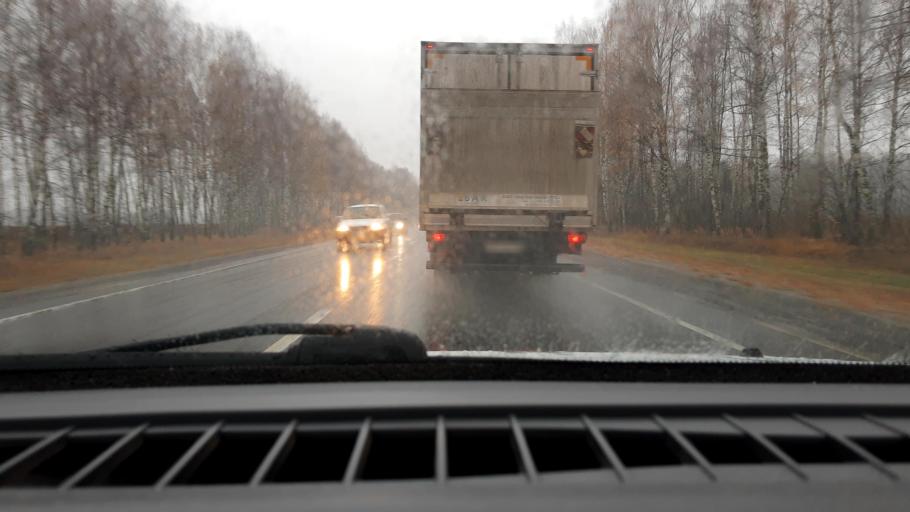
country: RU
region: Nizjnij Novgorod
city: Linda
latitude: 56.5615
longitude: 44.0246
